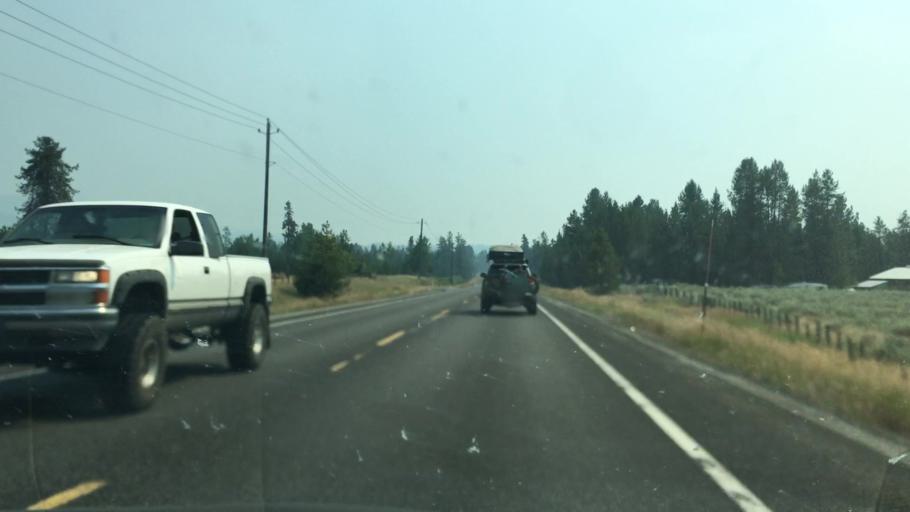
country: US
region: Idaho
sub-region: Valley County
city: Cascade
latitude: 44.4153
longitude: -115.9998
